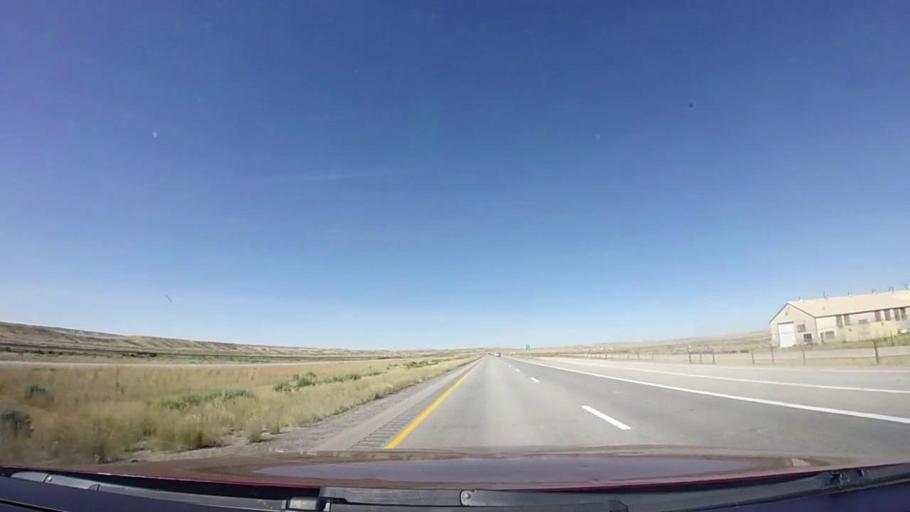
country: US
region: Wyoming
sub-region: Carbon County
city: Rawlins
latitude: 41.6529
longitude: -108.1233
